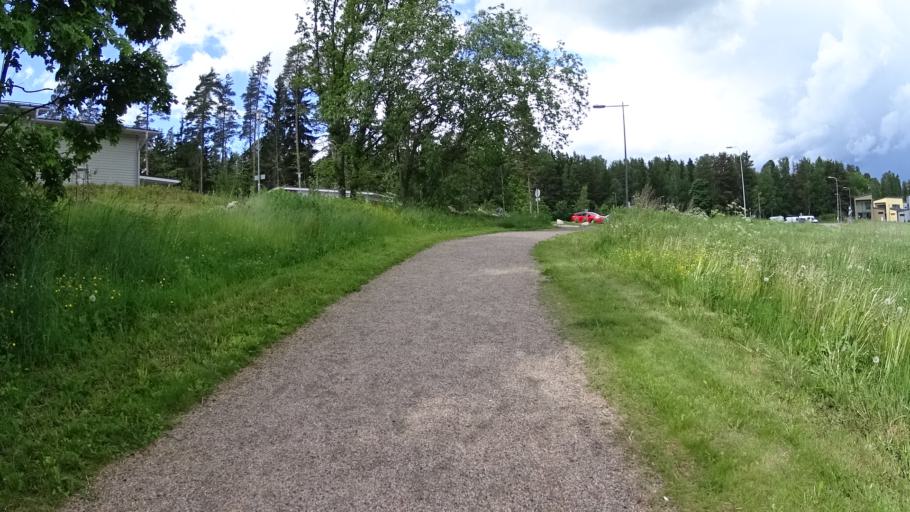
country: FI
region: Uusimaa
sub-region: Helsinki
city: Kauniainen
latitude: 60.2289
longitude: 24.6961
